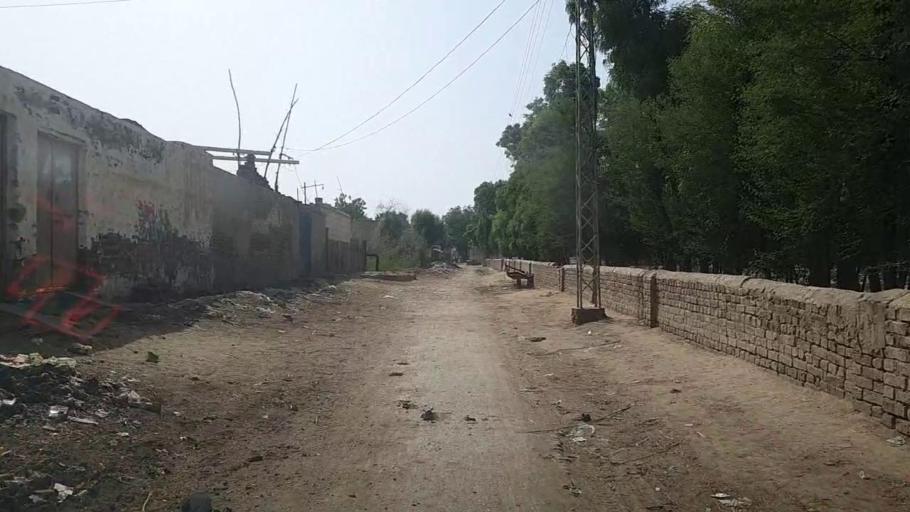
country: PK
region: Sindh
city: Pad Idan
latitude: 26.7728
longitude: 68.3048
